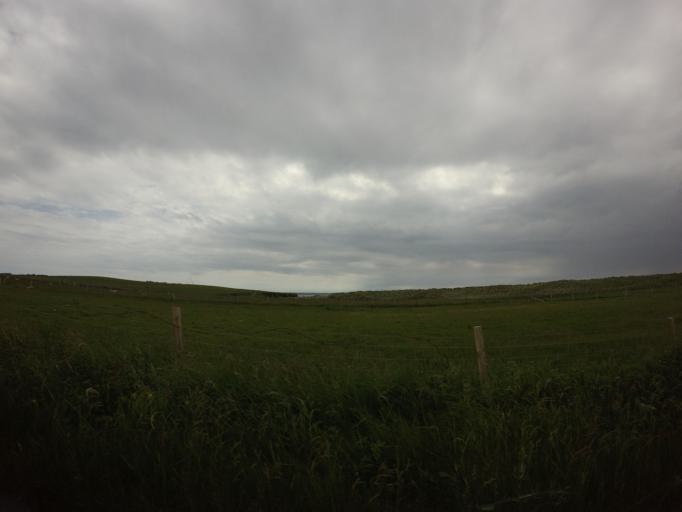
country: GB
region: Scotland
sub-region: Eilean Siar
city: Isle of Lewis
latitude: 58.2706
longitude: -6.3190
